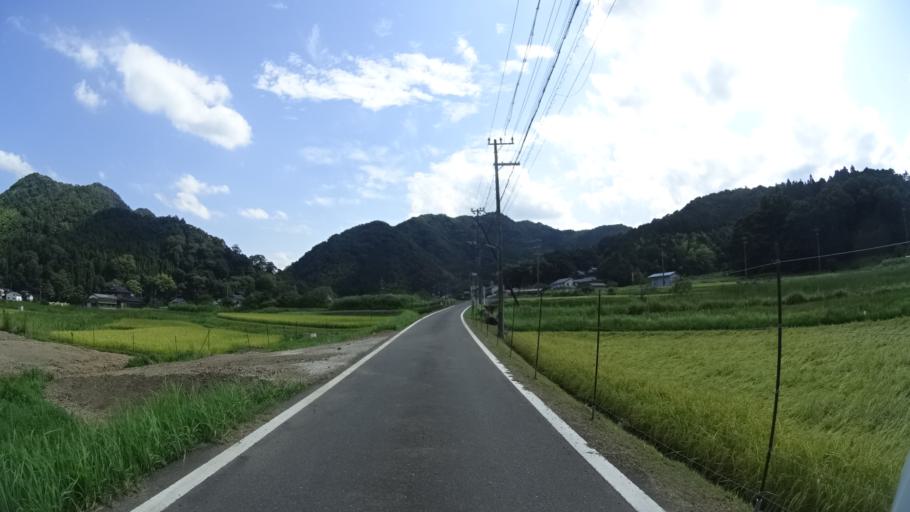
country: JP
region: Kyoto
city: Maizuru
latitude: 35.4320
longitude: 135.2964
